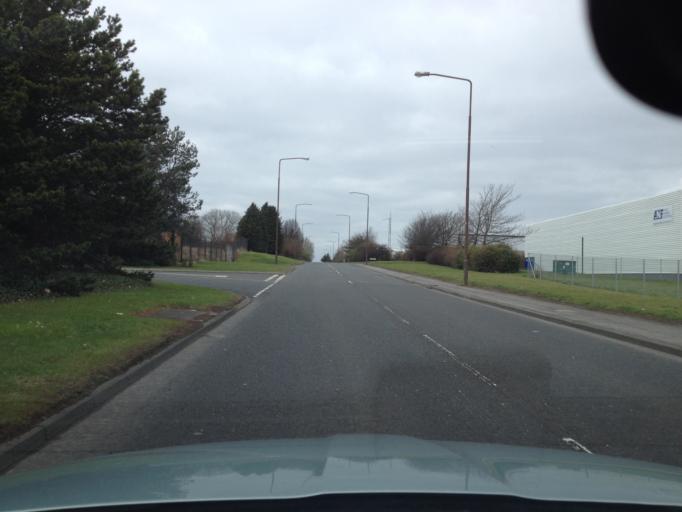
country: GB
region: Scotland
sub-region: West Lothian
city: Livingston
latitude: 55.9098
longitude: -3.5055
